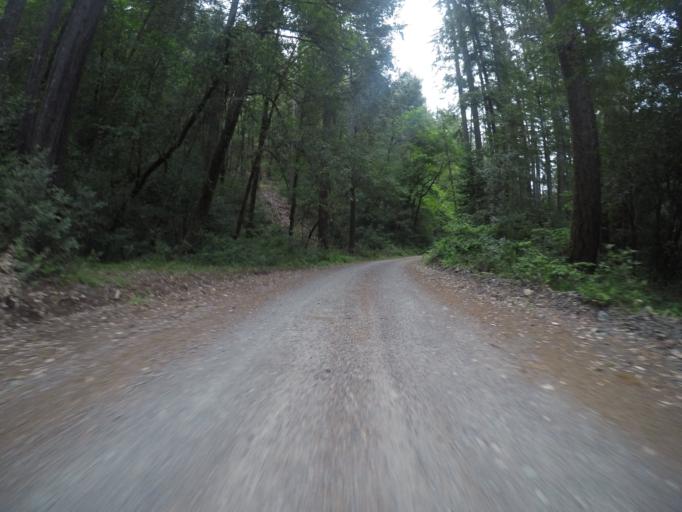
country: US
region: California
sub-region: Del Norte County
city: Bertsch-Oceanview
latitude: 41.7315
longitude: -123.8894
